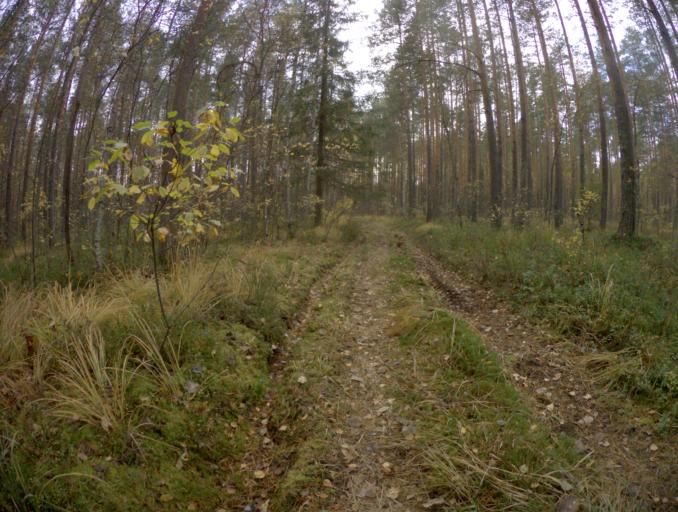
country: RU
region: Vladimir
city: Raduzhnyy
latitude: 55.9418
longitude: 40.3247
